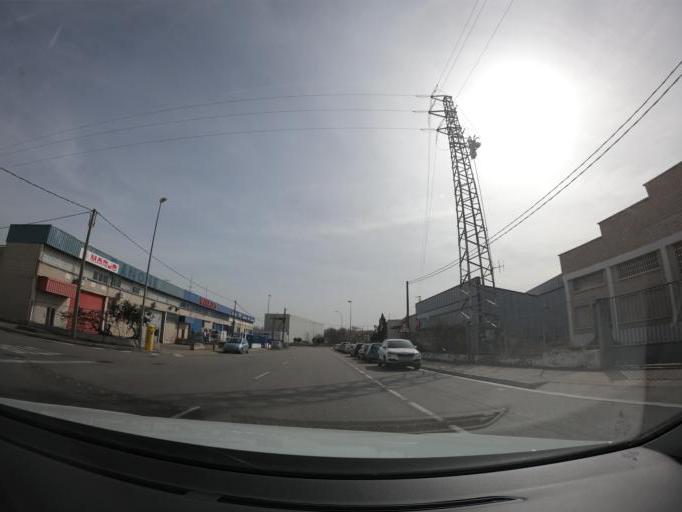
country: ES
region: Basque Country
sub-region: Provincia de Alava
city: Oyon
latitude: 42.4752
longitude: -2.4031
